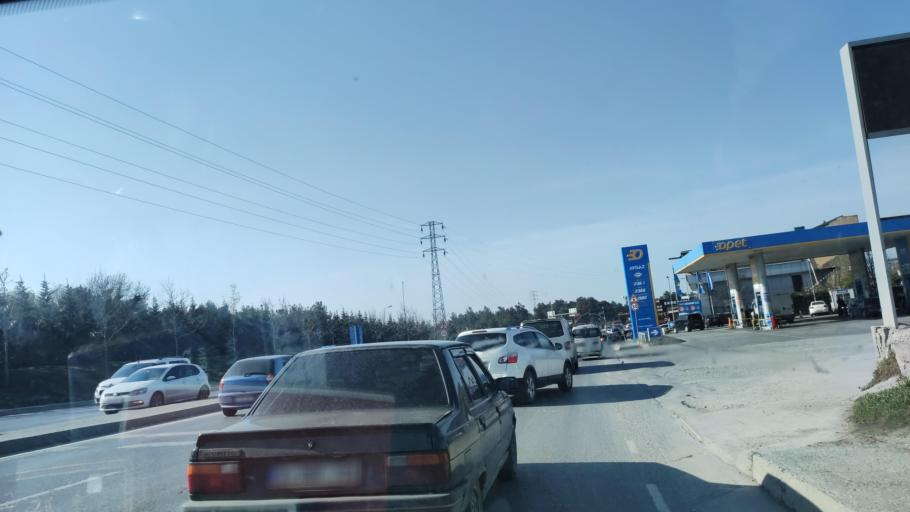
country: TR
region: Istanbul
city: Basaksehir
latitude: 41.1507
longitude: 28.7879
